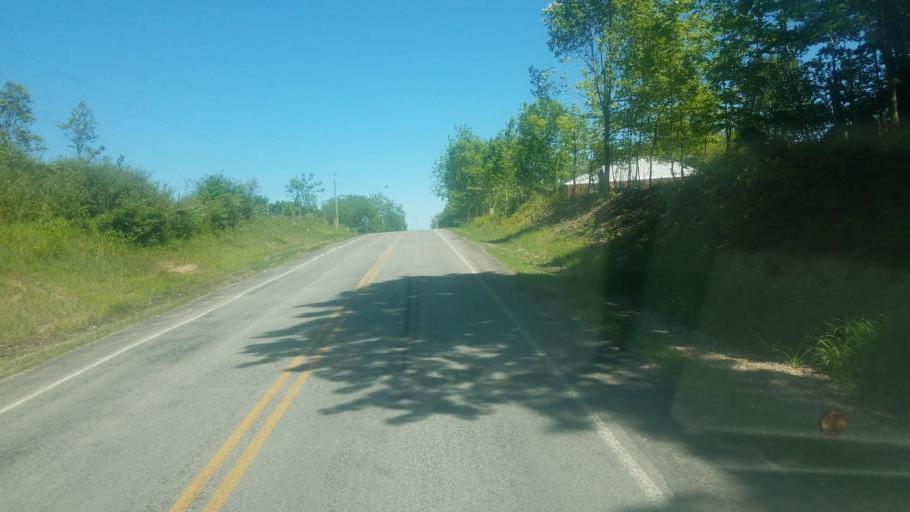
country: US
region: Ohio
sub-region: Champaign County
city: Saint Paris
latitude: 40.1749
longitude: -83.9624
